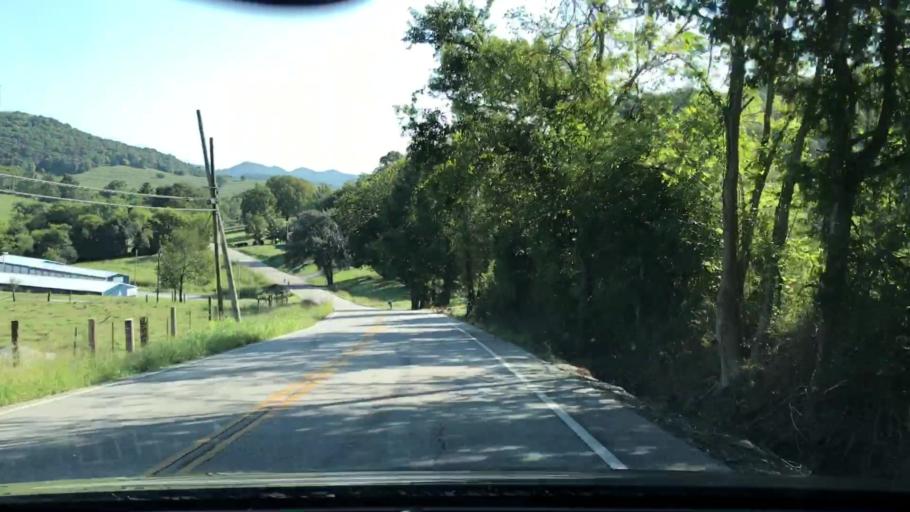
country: US
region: Tennessee
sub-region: Smith County
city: Carthage
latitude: 36.2735
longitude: -85.9551
